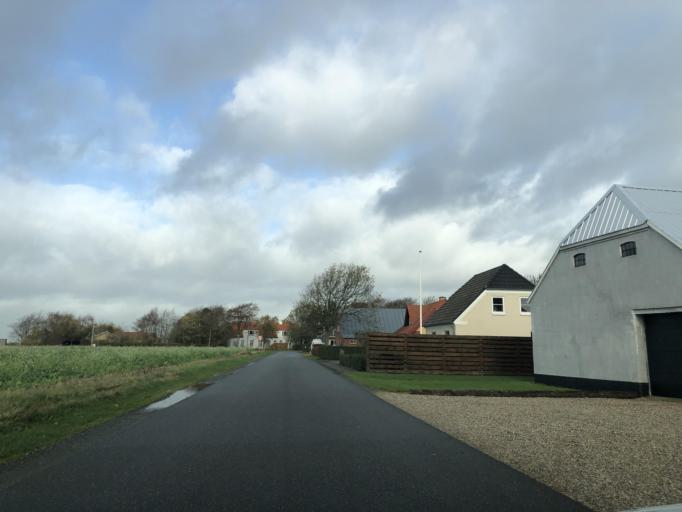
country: DK
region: South Denmark
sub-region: Esbjerg Kommune
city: Bramming
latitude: 55.4312
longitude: 8.6841
